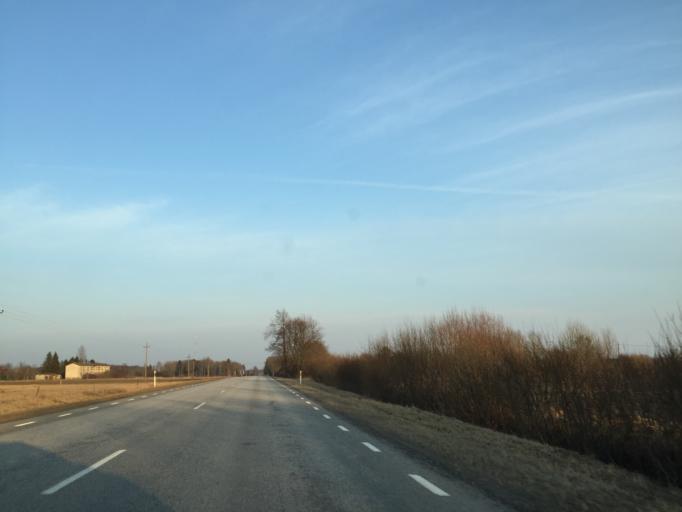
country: EE
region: Laeaene
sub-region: Lihula vald
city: Lihula
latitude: 58.5351
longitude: 24.0291
